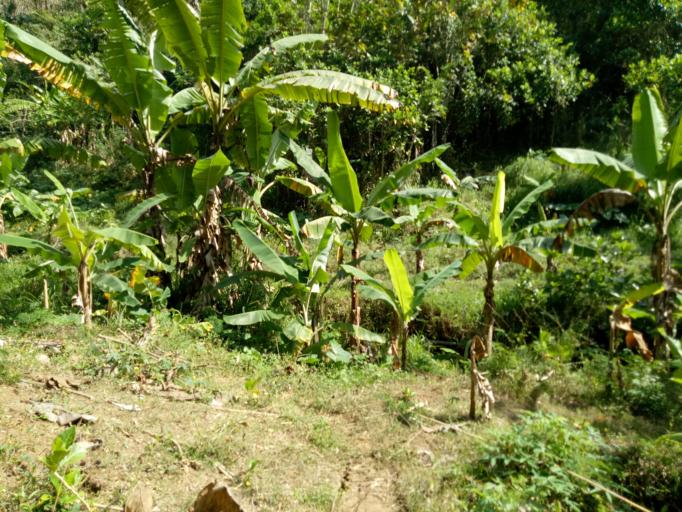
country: ID
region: East Java
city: Pagak
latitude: -8.2071
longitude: 112.5311
